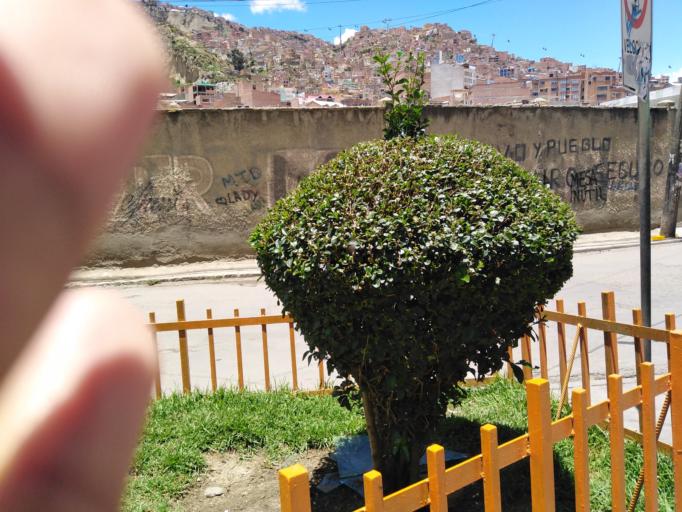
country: BO
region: La Paz
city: La Paz
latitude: -16.5128
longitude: -68.1407
